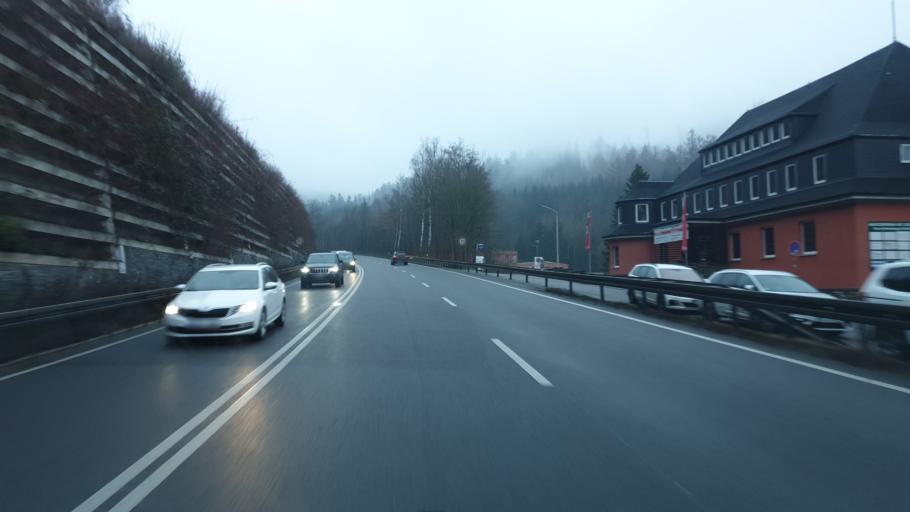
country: DE
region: Saxony
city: Zschopau
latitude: 50.7376
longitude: 13.0668
